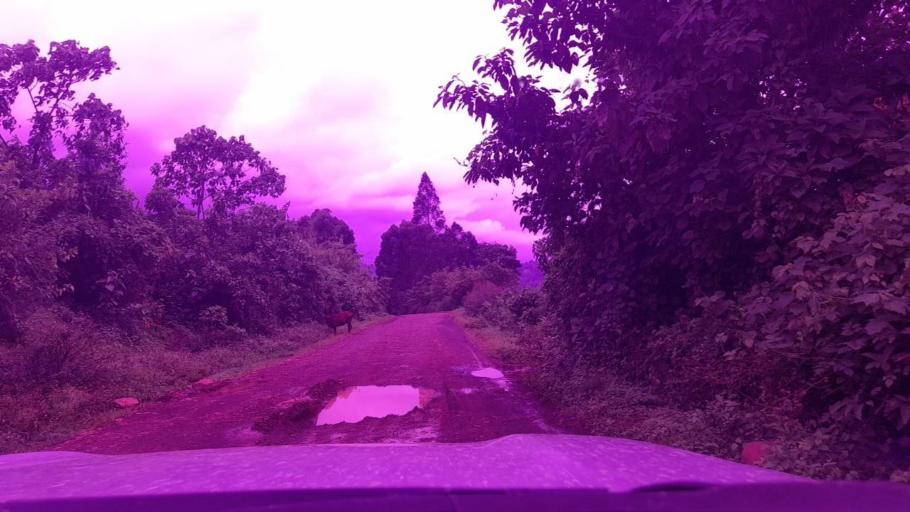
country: ET
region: Southern Nations, Nationalities, and People's Region
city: Tippi
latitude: 7.6335
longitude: 35.5754
